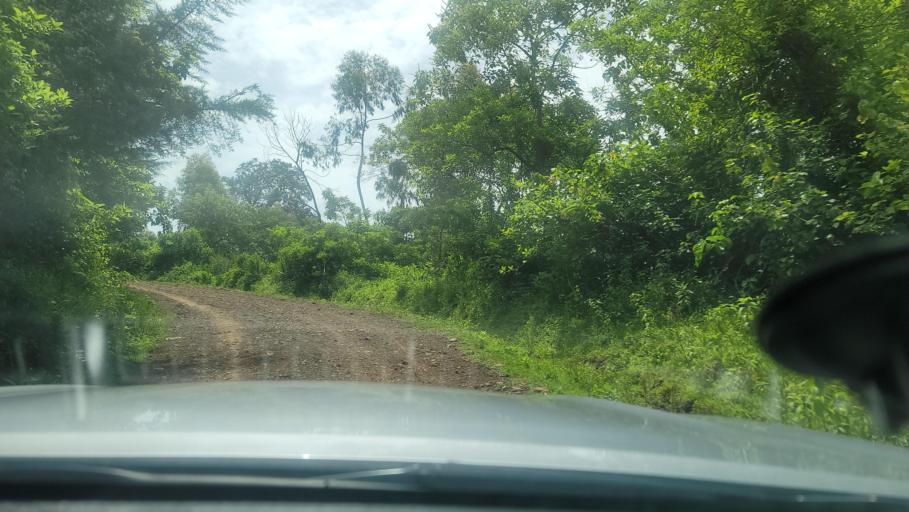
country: ET
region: Oromiya
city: Agaro
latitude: 7.8104
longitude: 36.4115
